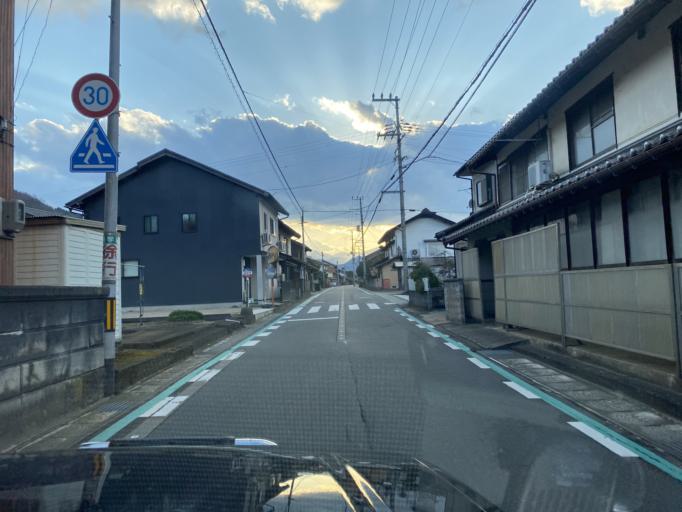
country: JP
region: Hyogo
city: Toyooka
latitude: 35.4643
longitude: 134.7596
